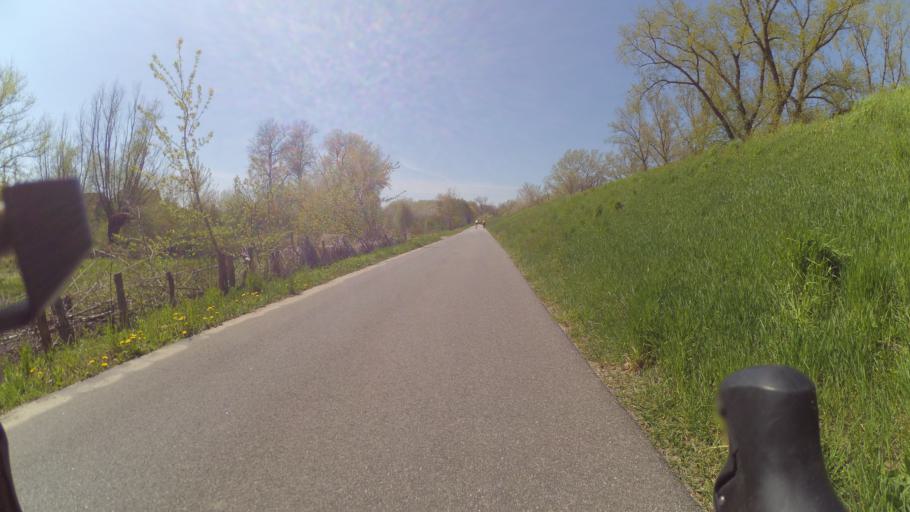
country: PL
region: Masovian Voivodeship
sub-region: Powiat plonski
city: Zaluski
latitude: 52.4194
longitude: 20.5196
